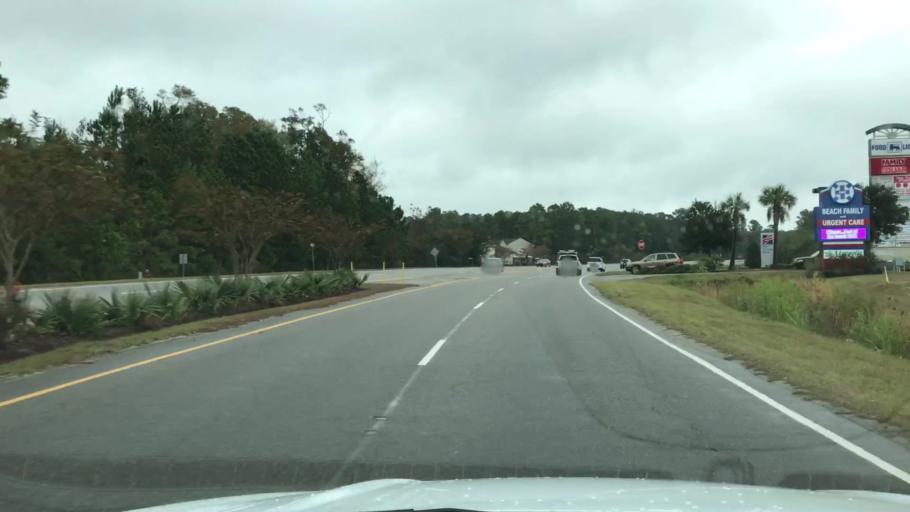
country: US
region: South Carolina
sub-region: Horry County
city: Myrtle Beach
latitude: 33.7547
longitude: -78.8671
